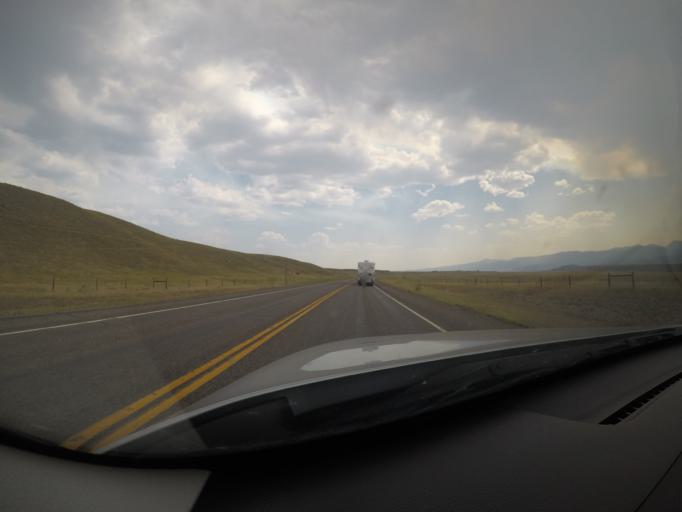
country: US
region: Montana
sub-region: Gallatin County
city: Big Sky
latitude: 45.1007
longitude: -111.6494
